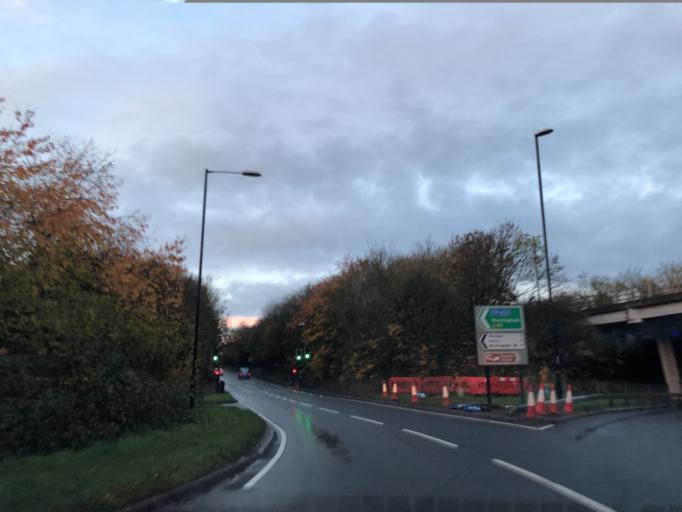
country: GB
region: England
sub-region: Coventry
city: Keresley
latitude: 52.4221
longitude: -1.5710
